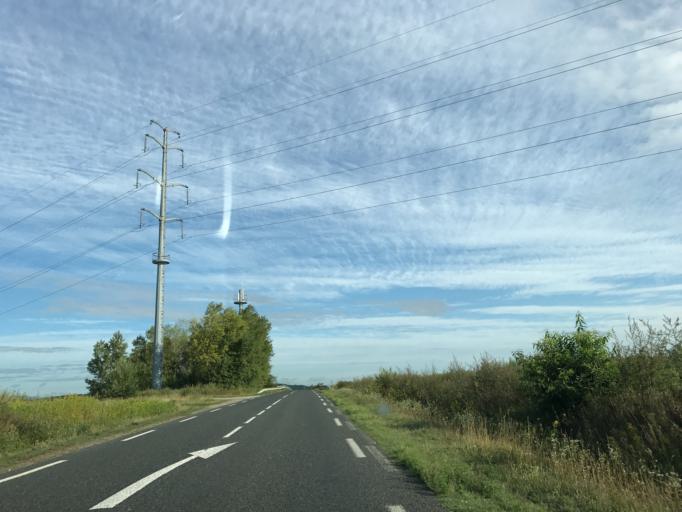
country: FR
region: Rhone-Alpes
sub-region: Departement de l'Ain
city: Miribel
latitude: 45.8555
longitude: 4.9282
